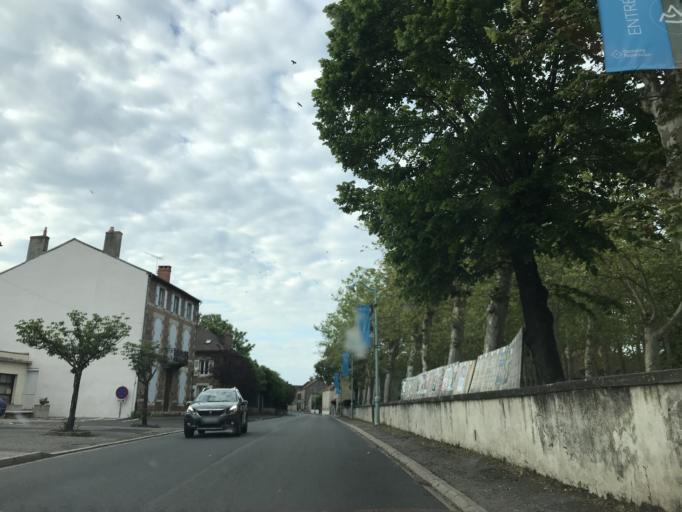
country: FR
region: Auvergne
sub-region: Departement du Puy-de-Dome
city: Randan
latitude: 46.0156
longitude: 3.3546
